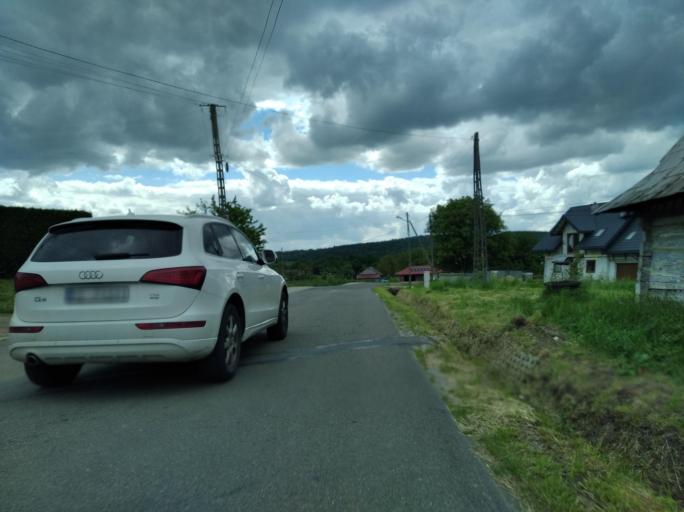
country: PL
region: Subcarpathian Voivodeship
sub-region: Powiat brzozowski
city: Jablonica Polska
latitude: 49.7031
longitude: 21.8958
